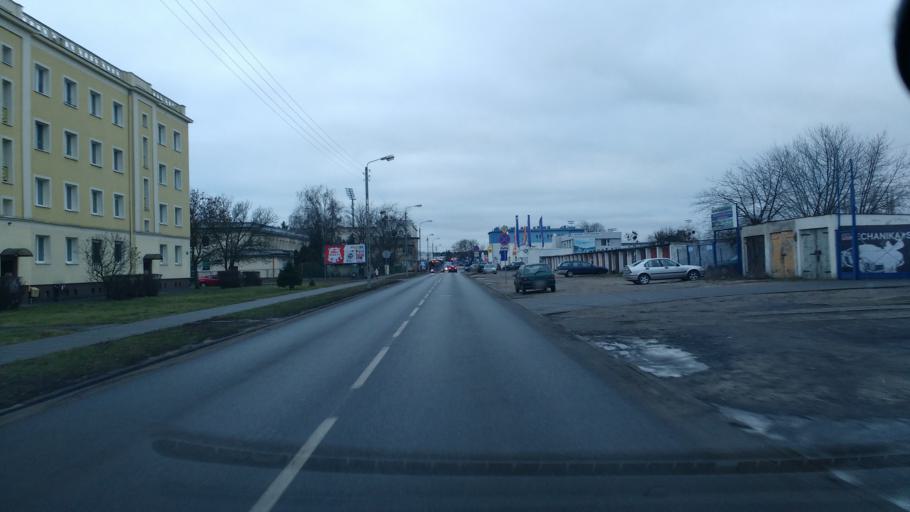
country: PL
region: Kujawsko-Pomorskie
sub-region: Bydgoszcz
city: Bydgoszcz
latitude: 53.1444
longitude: 18.0282
